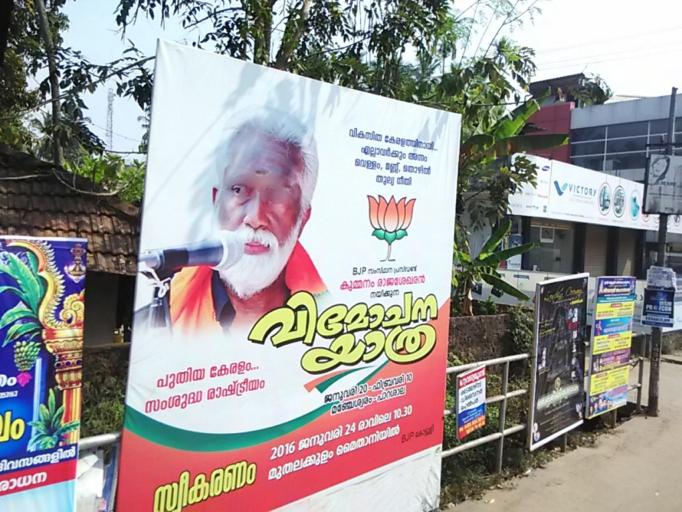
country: IN
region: Kerala
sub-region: Kozhikode
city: Kozhikode
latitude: 11.2582
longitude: 75.8003
